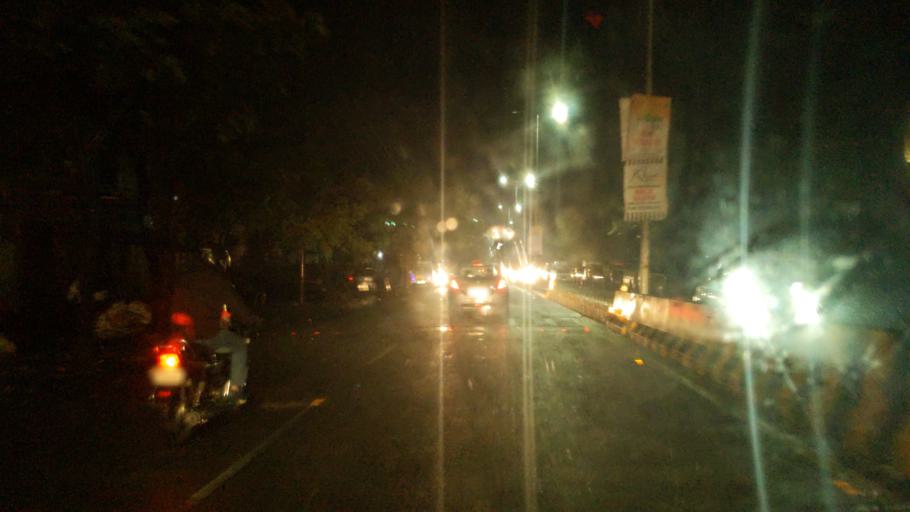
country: IN
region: Uttarakhand
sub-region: Naini Tal
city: Haldwani
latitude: 29.2561
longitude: 79.5426
